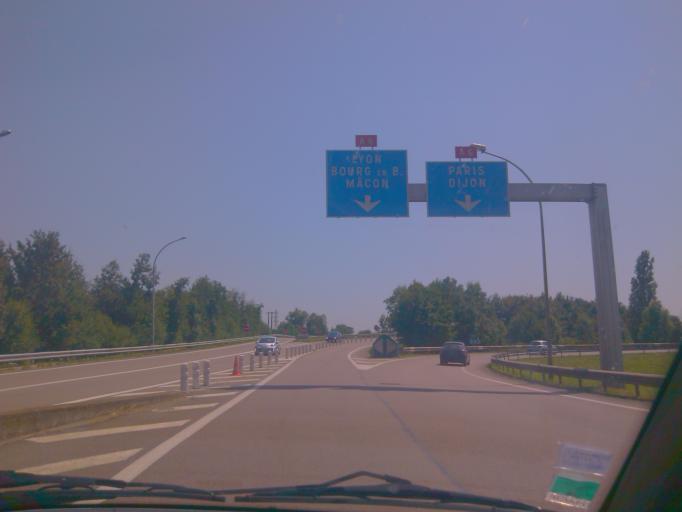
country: FR
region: Bourgogne
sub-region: Departement de Saone-et-Loire
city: Saint-Remy
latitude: 46.7537
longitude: 4.8333
